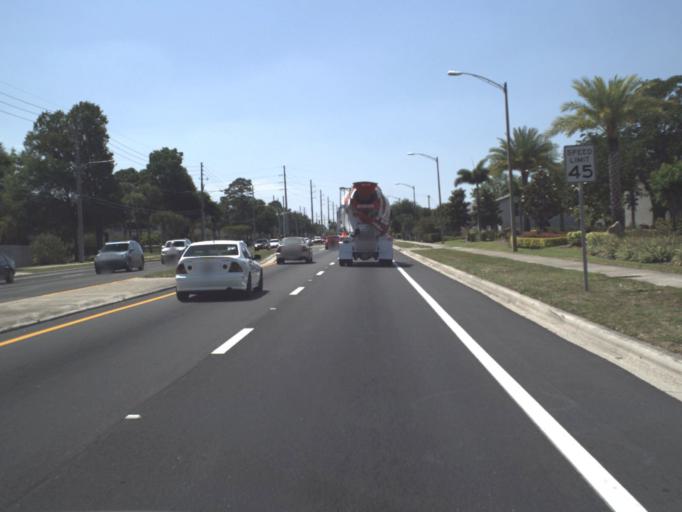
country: US
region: Florida
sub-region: Orange County
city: Azalea Park
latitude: 28.5194
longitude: -81.2990
